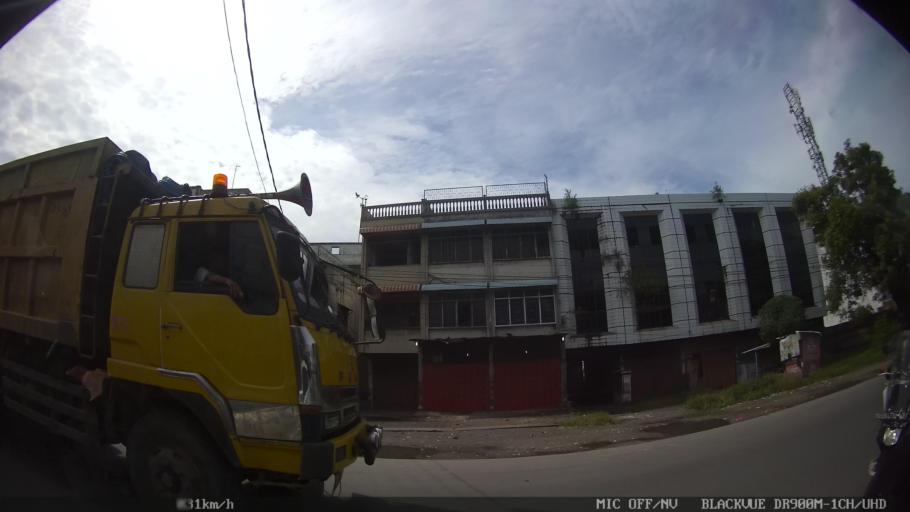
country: ID
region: North Sumatra
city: Medan
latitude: 3.6269
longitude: 98.6609
